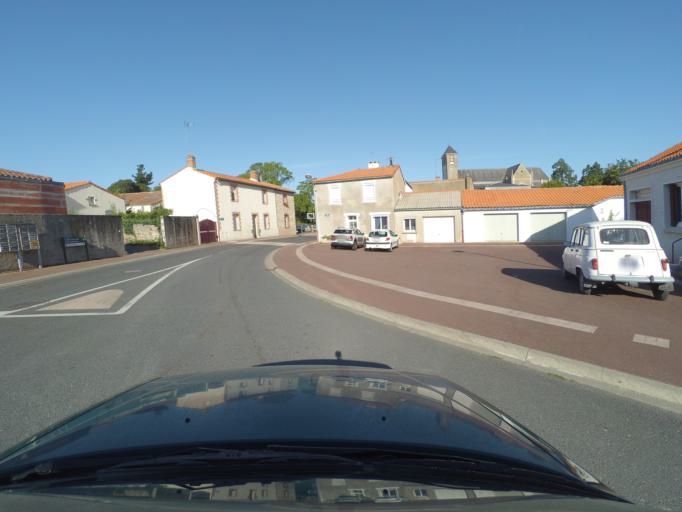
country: FR
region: Pays de la Loire
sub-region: Departement de la Loire-Atlantique
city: Le Bignon
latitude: 47.0977
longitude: -1.4876
